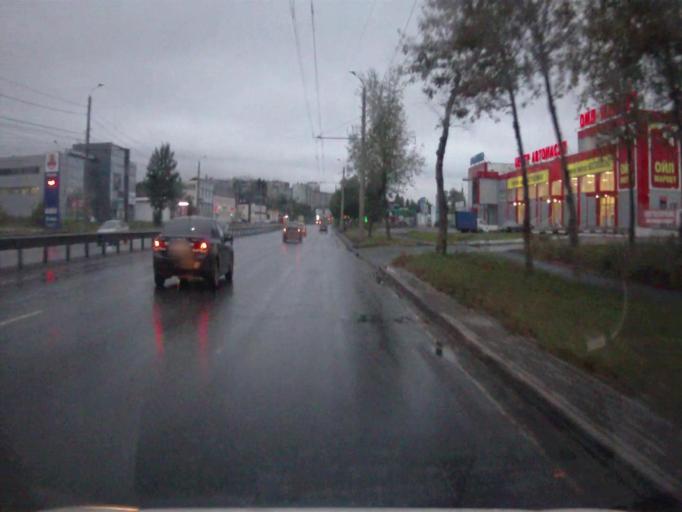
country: RU
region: Chelyabinsk
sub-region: Gorod Chelyabinsk
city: Chelyabinsk
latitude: 55.1376
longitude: 61.4601
